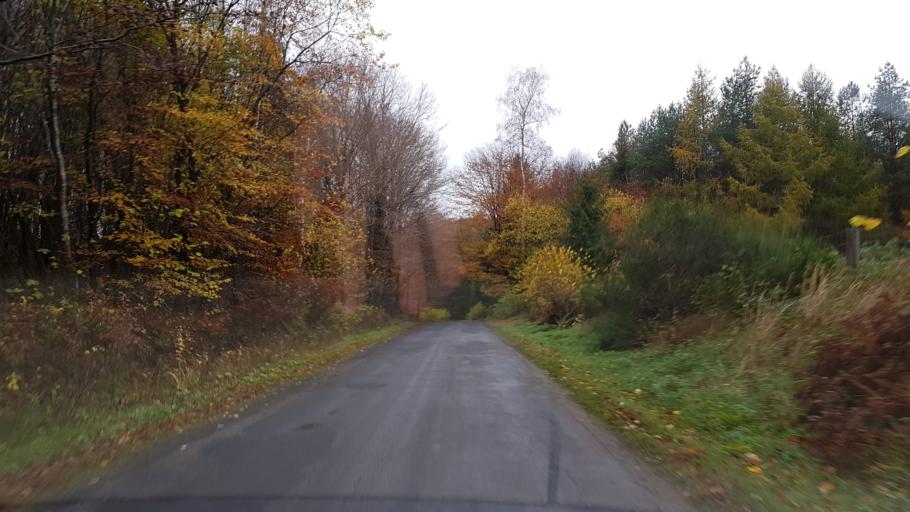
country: PL
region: West Pomeranian Voivodeship
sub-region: Powiat koszalinski
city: Polanow
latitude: 54.0789
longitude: 16.5790
